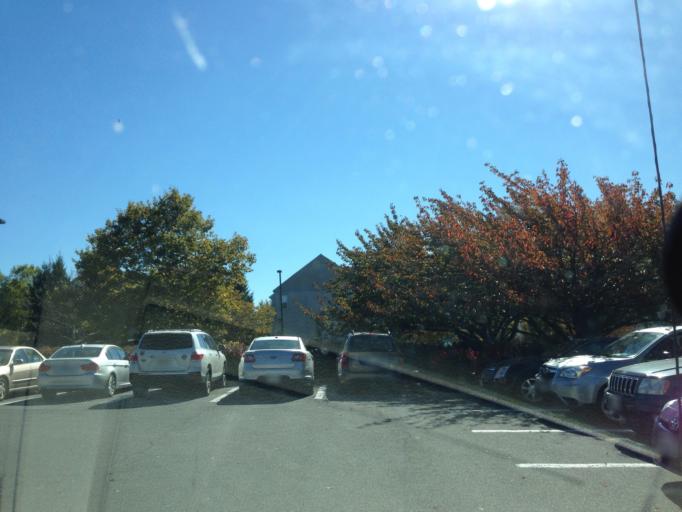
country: US
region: Maryland
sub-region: Montgomery County
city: Germantown
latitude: 39.1978
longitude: -77.2497
